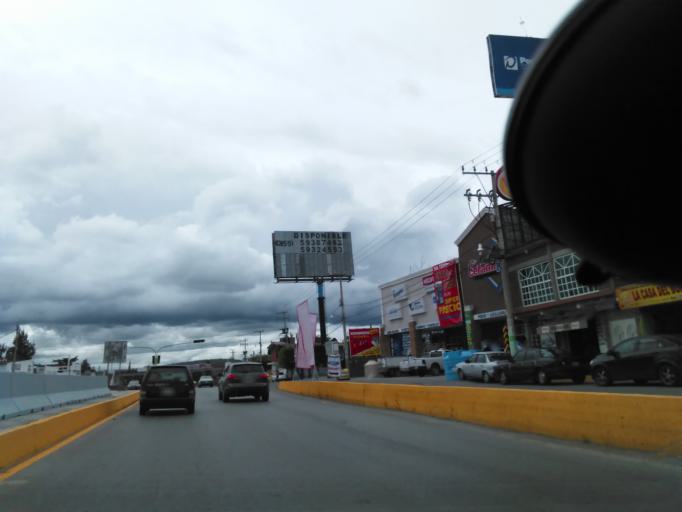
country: MX
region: Hidalgo
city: El Llano
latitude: 20.0536
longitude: -99.3152
